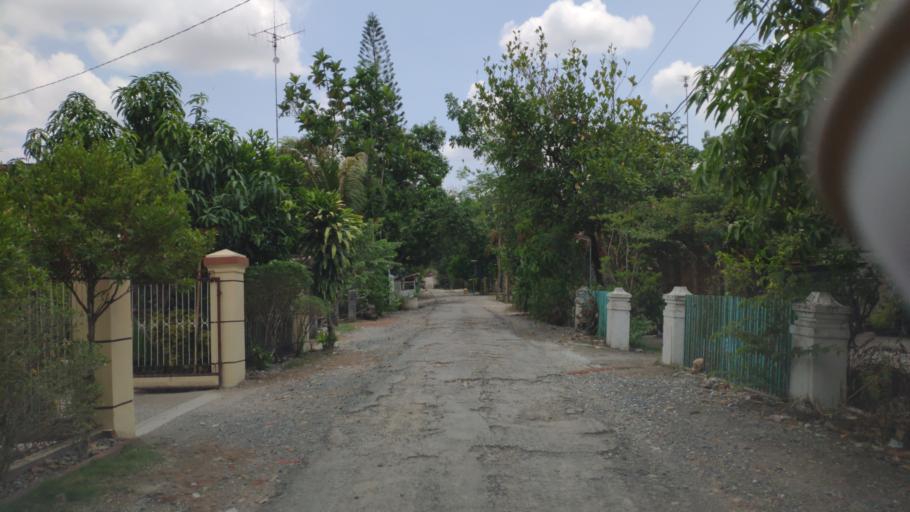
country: ID
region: Central Java
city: Gumiring
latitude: -7.0393
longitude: 111.3892
